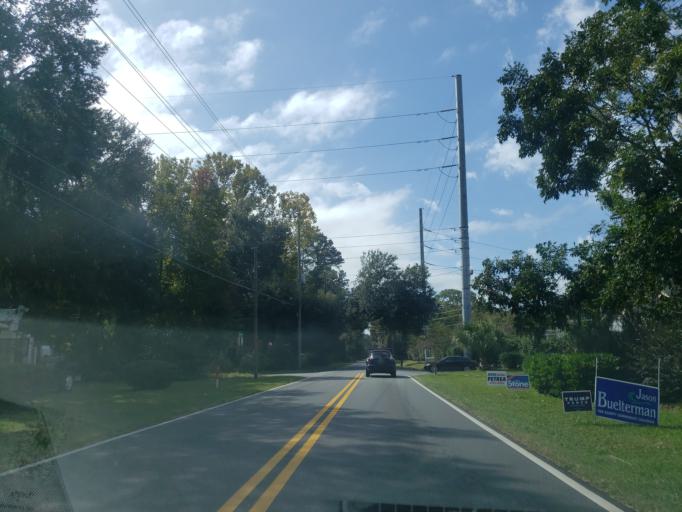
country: US
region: Georgia
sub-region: Chatham County
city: Montgomery
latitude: 31.9502
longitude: -81.1057
